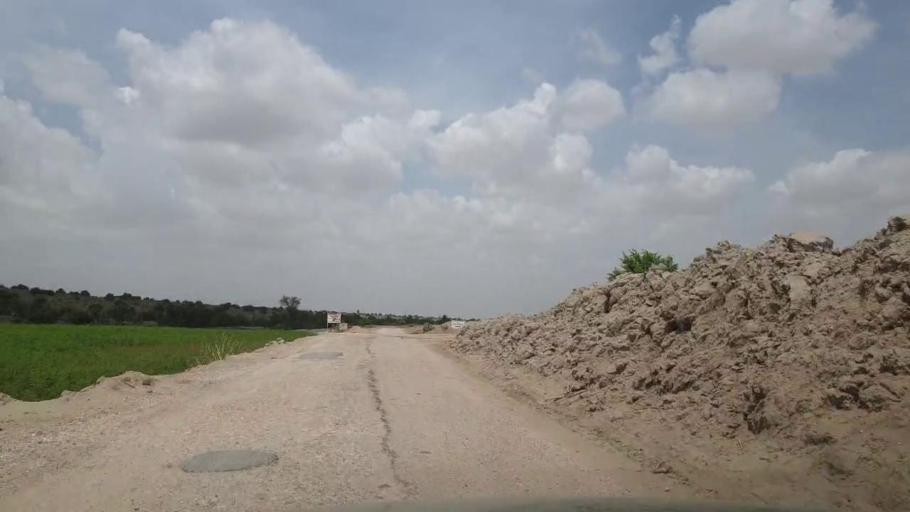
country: PK
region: Sindh
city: Kot Diji
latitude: 27.2164
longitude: 69.1004
